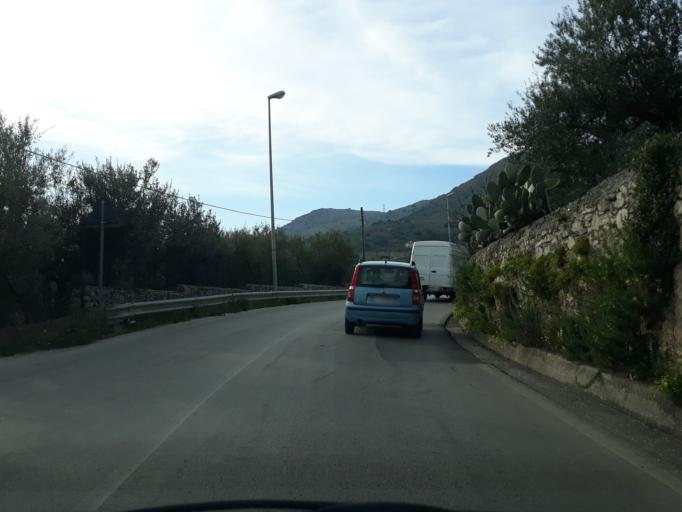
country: IT
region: Sicily
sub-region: Palermo
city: Giardinello
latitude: 38.0881
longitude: 13.1653
